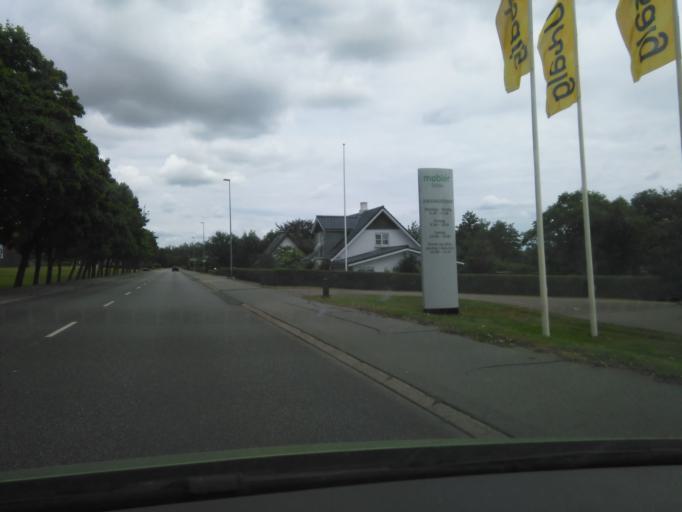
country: DK
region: Central Jutland
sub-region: Odder Kommune
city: Odder
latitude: 55.9864
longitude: 10.1540
